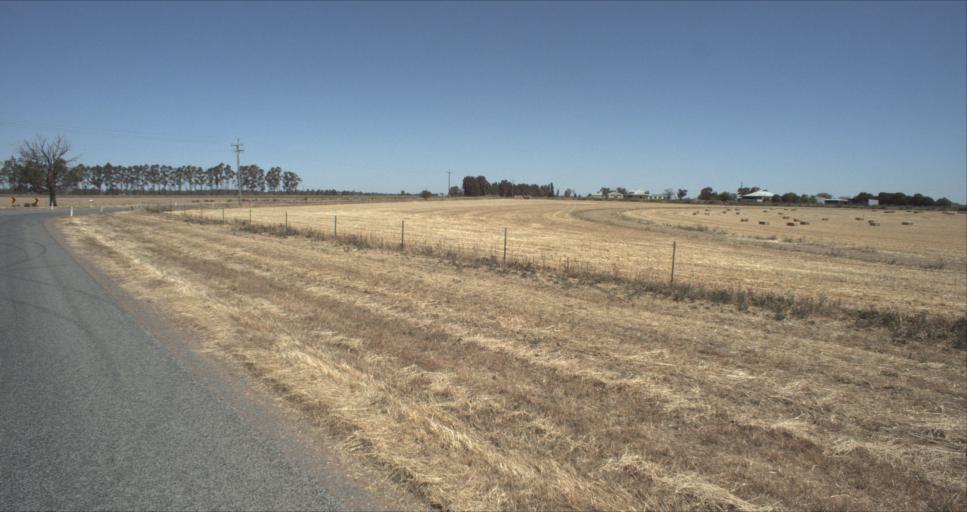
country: AU
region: New South Wales
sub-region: Leeton
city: Leeton
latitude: -34.5330
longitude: 146.4465
